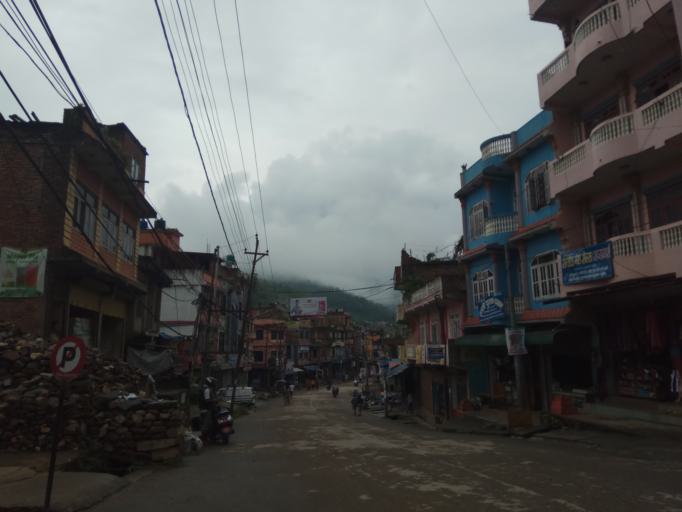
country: NP
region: Central Region
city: Kirtipur
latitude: 27.9114
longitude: 84.8894
